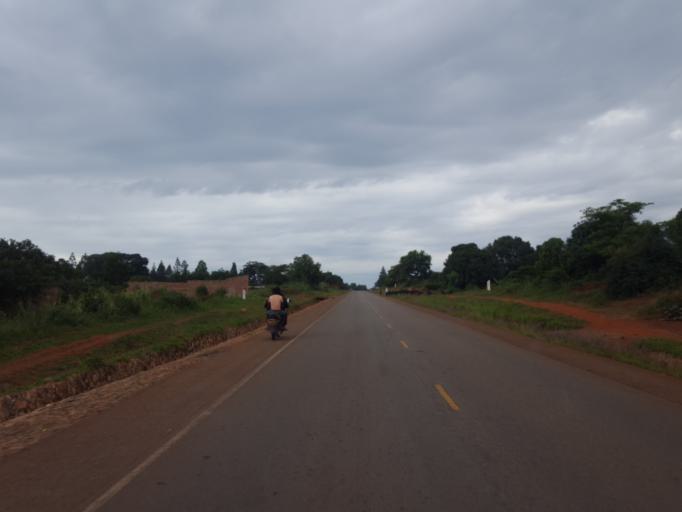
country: UG
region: Central Region
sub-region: Kiboga District
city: Kiboga
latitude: 1.0148
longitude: 31.6910
